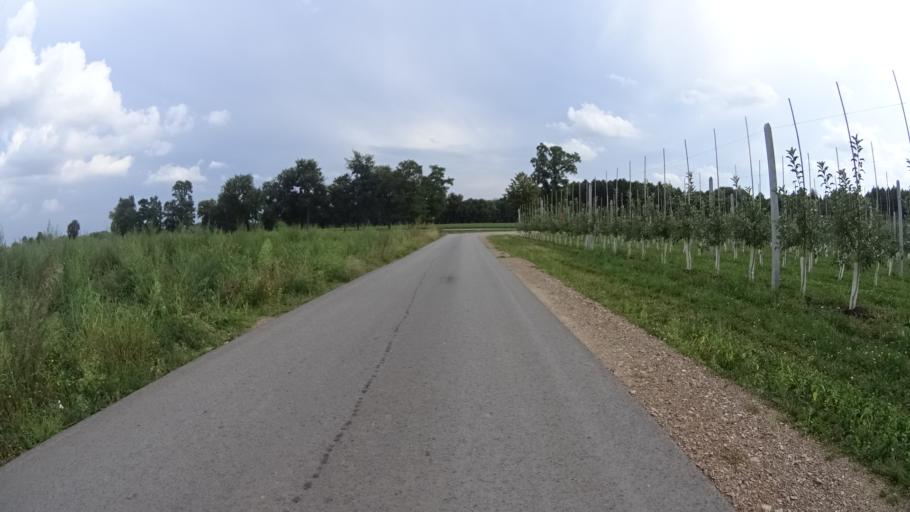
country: PL
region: Masovian Voivodeship
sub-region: Powiat grojecki
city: Goszczyn
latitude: 51.6960
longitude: 20.8213
